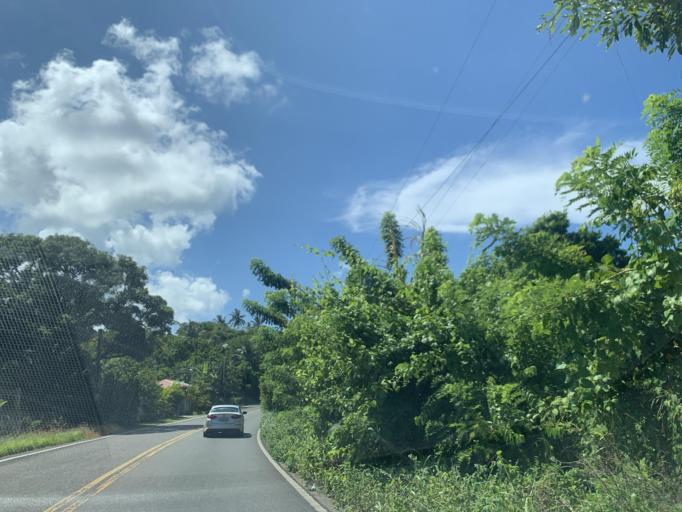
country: DO
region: Maria Trinidad Sanchez
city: Cabrera
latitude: 19.6485
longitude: -69.9273
